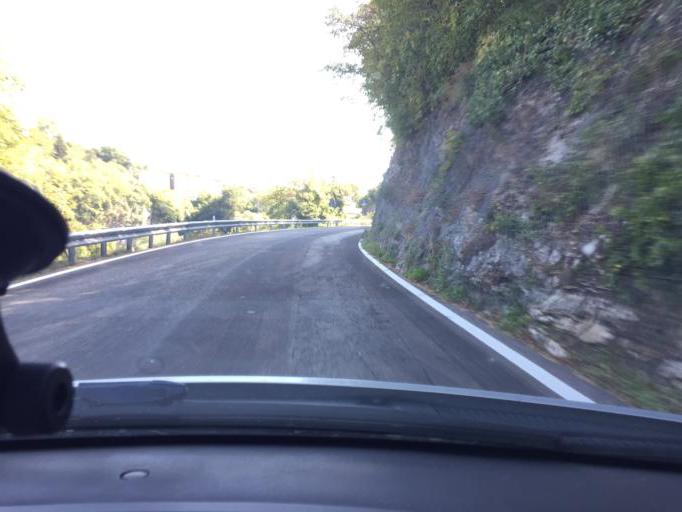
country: IT
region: Trentino-Alto Adige
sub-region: Provincia di Trento
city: Trento
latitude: 46.0675
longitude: 11.0975
